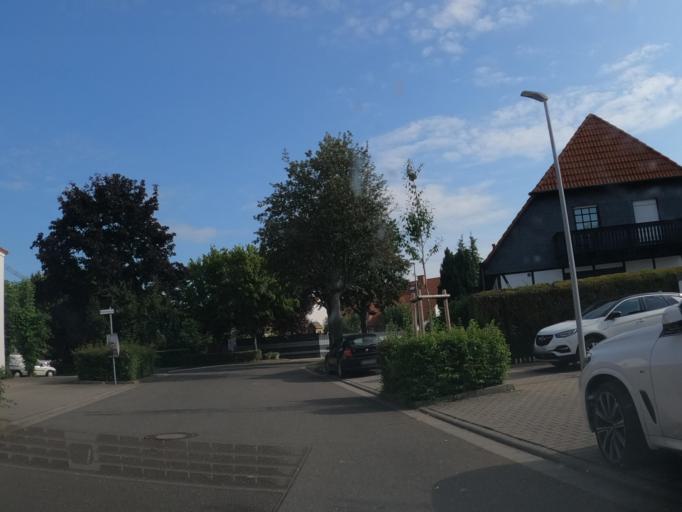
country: DE
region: Rheinland-Pfalz
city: Armsheim
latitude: 49.8125
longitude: 8.0603
